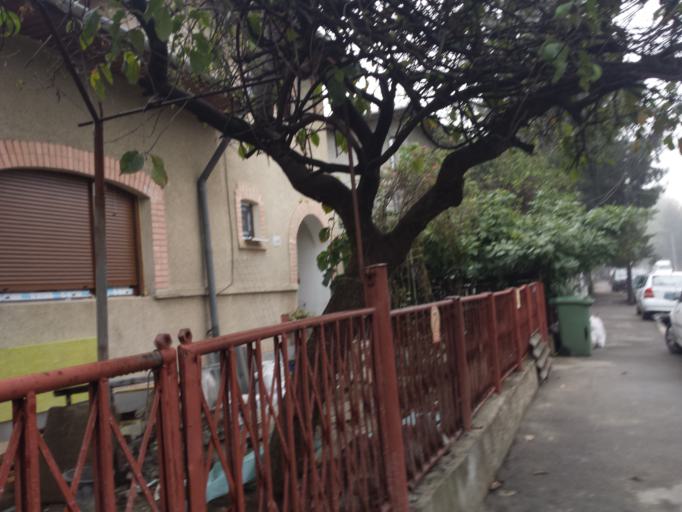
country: RO
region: Ilfov
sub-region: Comuna Chiajna
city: Rosu
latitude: 44.4709
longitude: 26.0601
